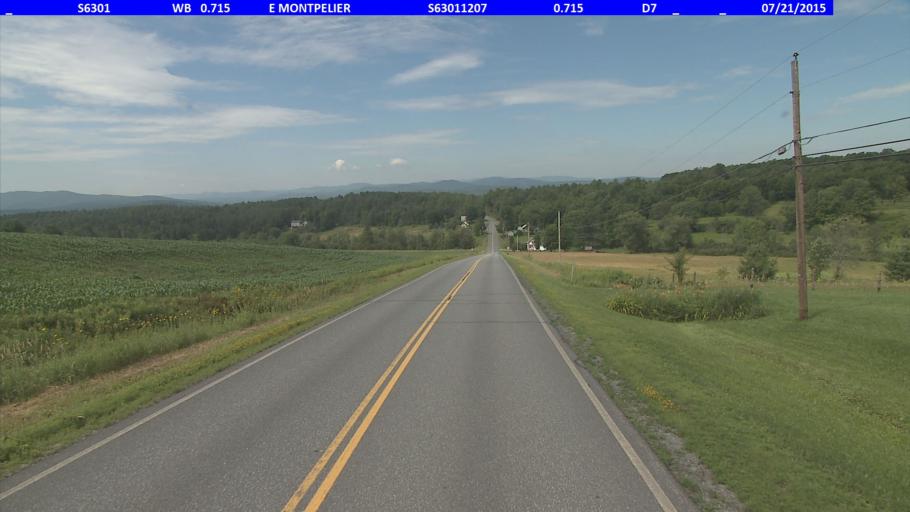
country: US
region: Vermont
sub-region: Washington County
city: Montpelier
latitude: 44.2777
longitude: -72.5410
